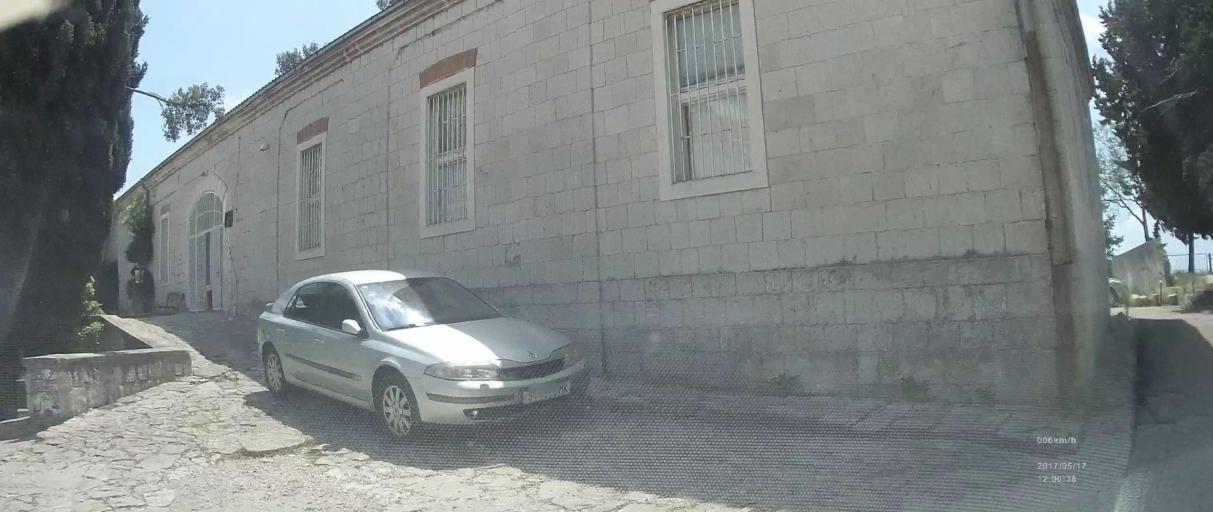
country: HR
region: Splitsko-Dalmatinska
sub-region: Grad Split
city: Split
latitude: 43.5086
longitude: 16.4468
